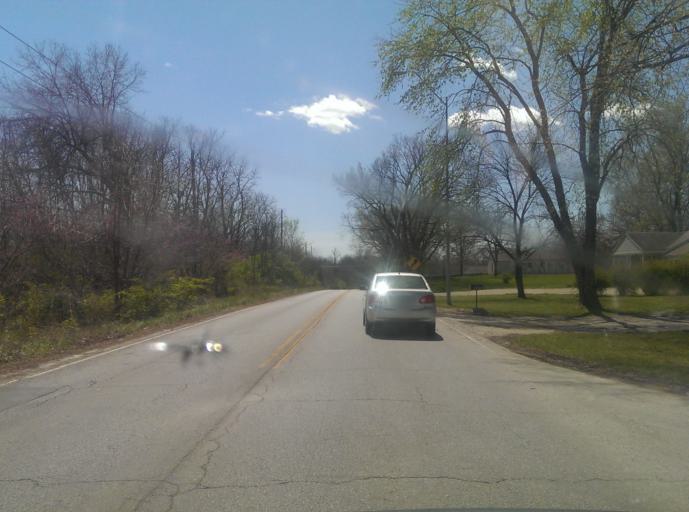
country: US
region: Missouri
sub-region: Jackson County
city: Grandview
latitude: 38.8983
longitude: -94.5854
